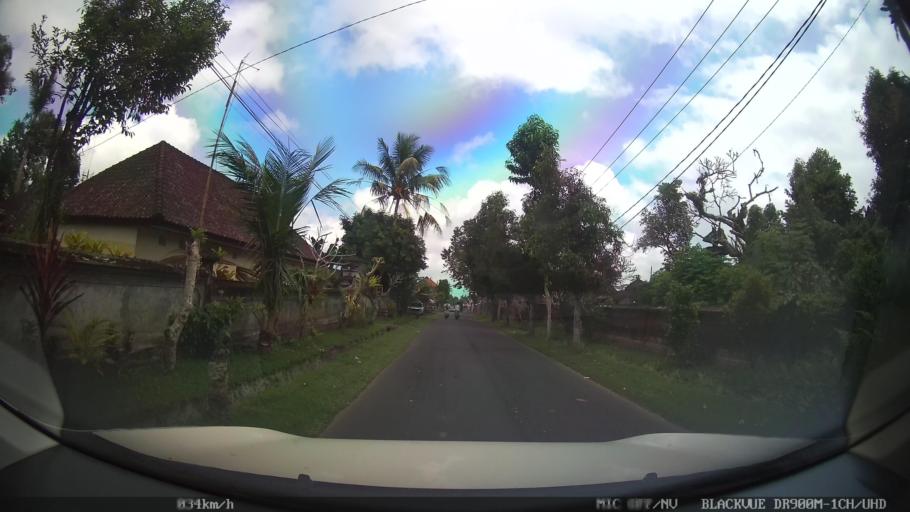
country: ID
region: Bali
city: Banjar Petak
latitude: -8.4499
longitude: 115.3186
